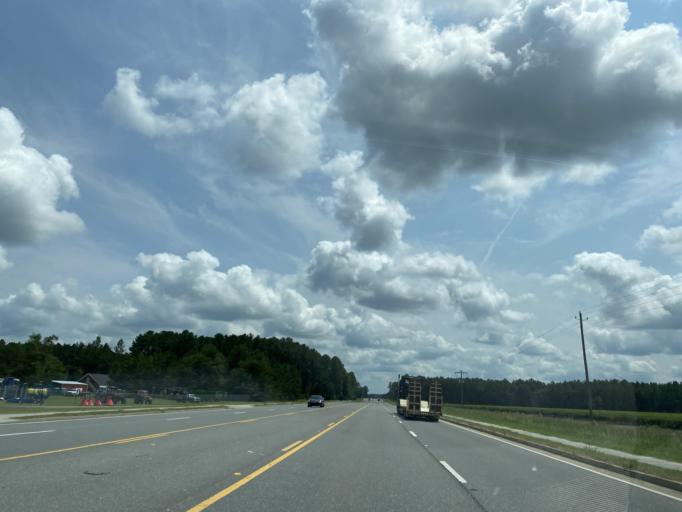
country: US
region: Georgia
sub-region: Ware County
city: Deenwood
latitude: 31.3496
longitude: -82.4638
